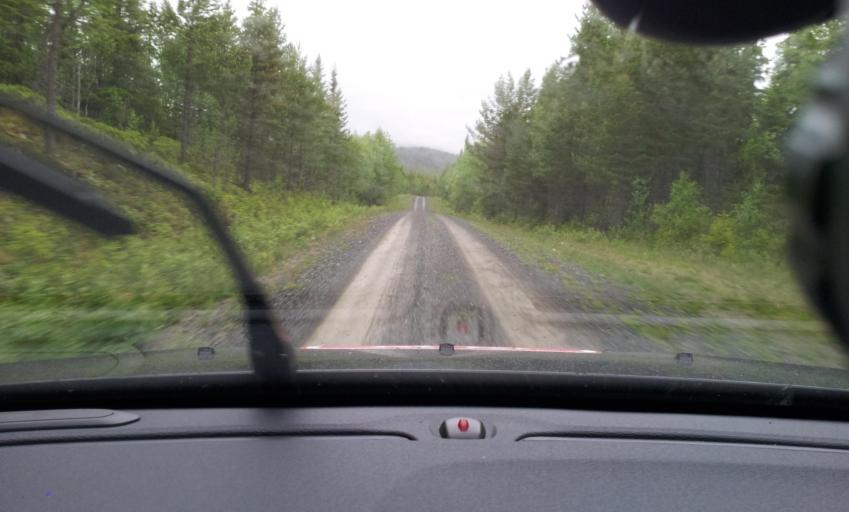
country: SE
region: Jaemtland
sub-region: Are Kommun
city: Jarpen
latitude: 63.1779
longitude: 13.4703
